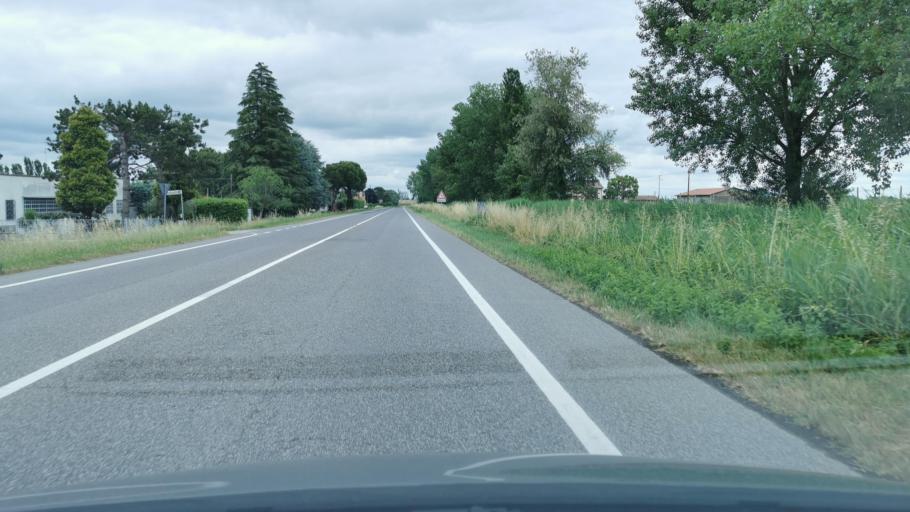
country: IT
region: Emilia-Romagna
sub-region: Provincia di Ravenna
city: Cotignola
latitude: 44.3929
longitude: 11.9573
